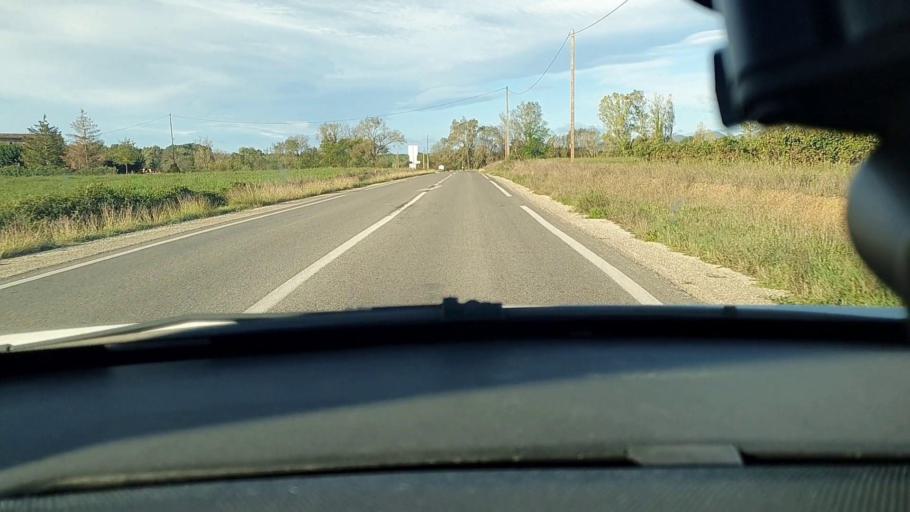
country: FR
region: Languedoc-Roussillon
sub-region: Departement du Gard
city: Saint-Ambroix
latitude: 44.2372
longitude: 4.2675
